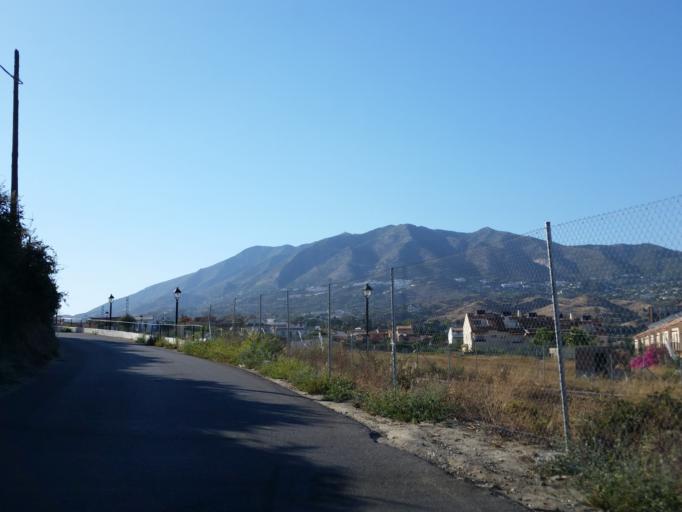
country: ES
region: Andalusia
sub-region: Provincia de Malaga
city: Fuengirola
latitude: 36.5599
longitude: -4.6217
